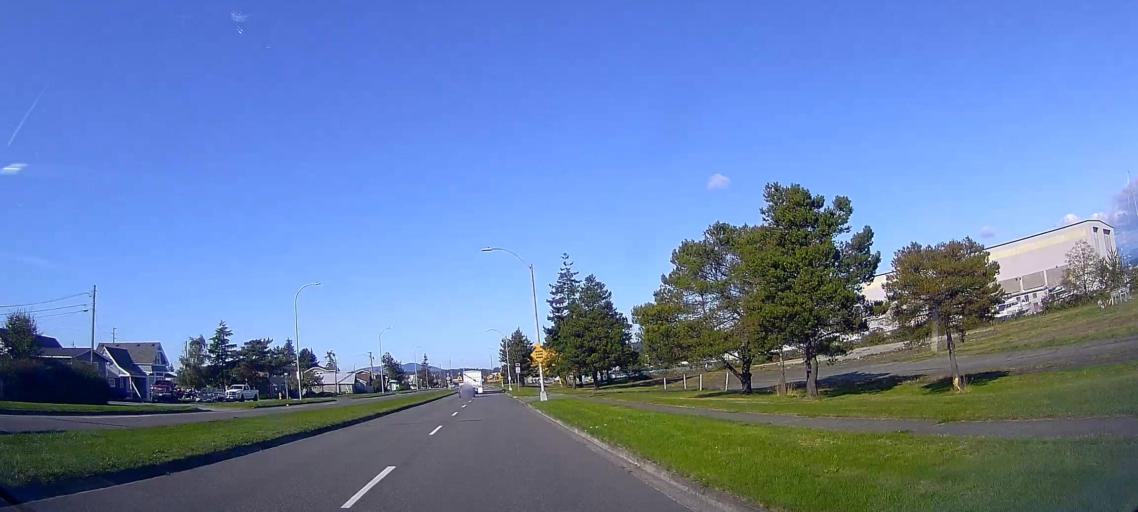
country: US
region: Washington
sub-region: Skagit County
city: Anacortes
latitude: 48.5021
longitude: -122.6095
